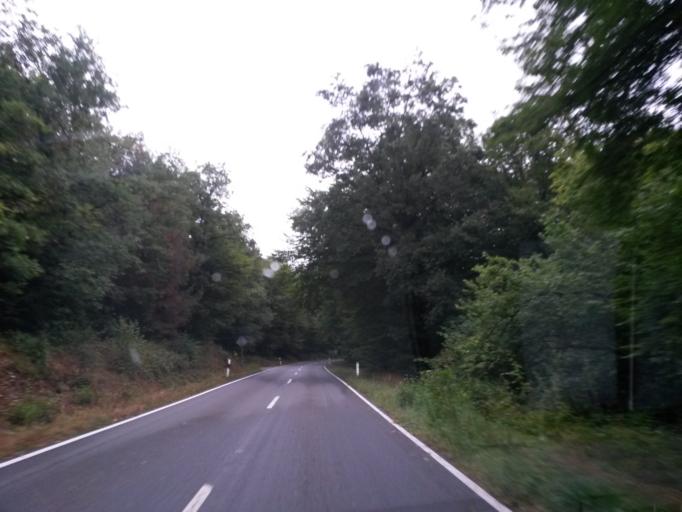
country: DE
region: North Rhine-Westphalia
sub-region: Regierungsbezirk Koln
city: Ruppichteroth
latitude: 50.8672
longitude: 7.5146
